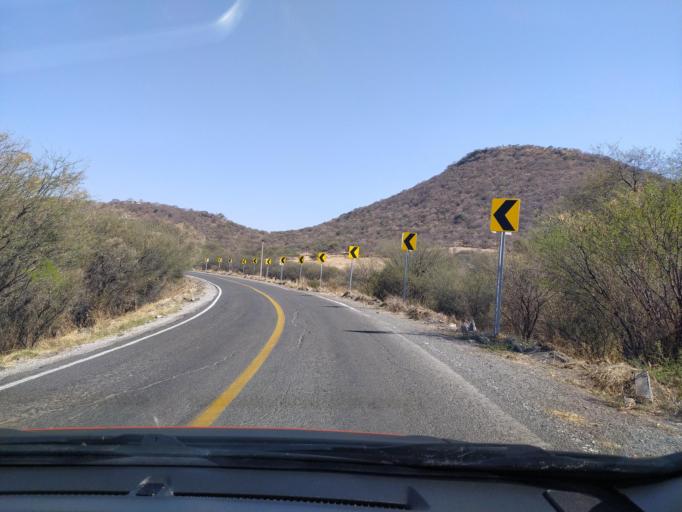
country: MX
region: Guanajuato
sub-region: San Francisco del Rincon
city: San Ignacio de Hidalgo
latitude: 20.7948
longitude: -101.8354
